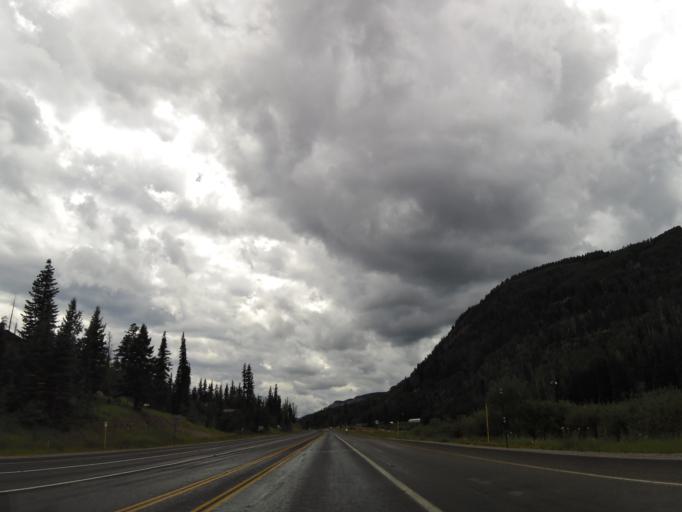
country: US
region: Colorado
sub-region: San Juan County
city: Silverton
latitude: 37.6279
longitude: -107.8101
